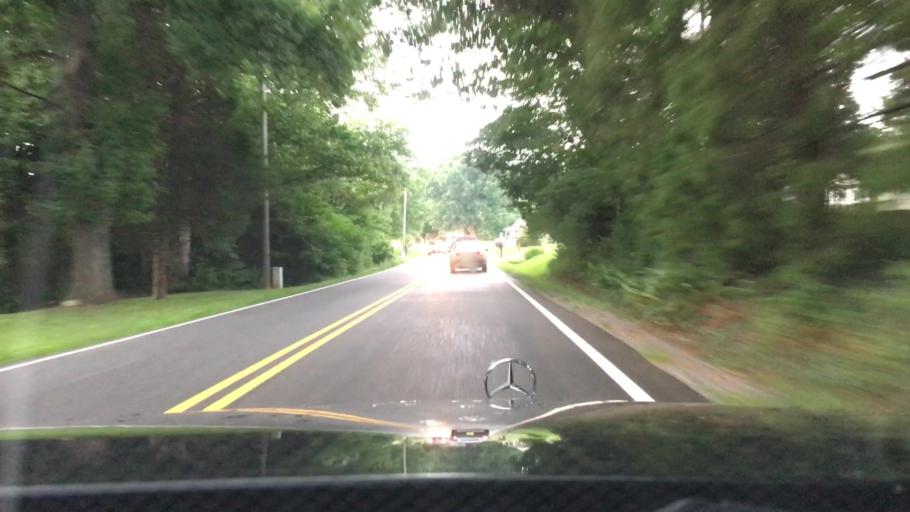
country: US
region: Virginia
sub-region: Campbell County
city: Timberlake
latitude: 37.2864
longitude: -79.2424
